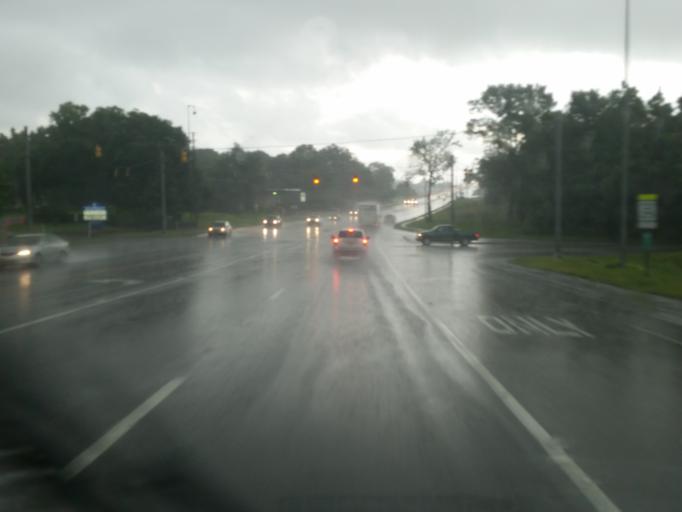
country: US
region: Alabama
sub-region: Mobile County
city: Prichard
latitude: 30.7315
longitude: -88.0608
